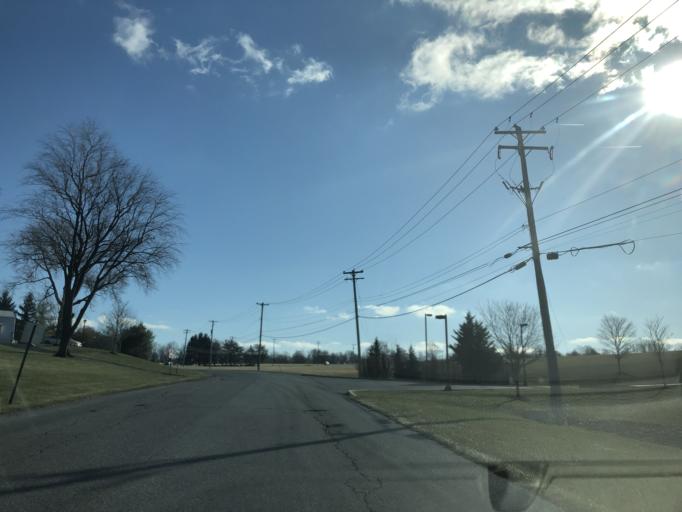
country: US
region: Pennsylvania
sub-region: Chester County
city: Coatesville
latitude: 39.9934
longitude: -75.8745
